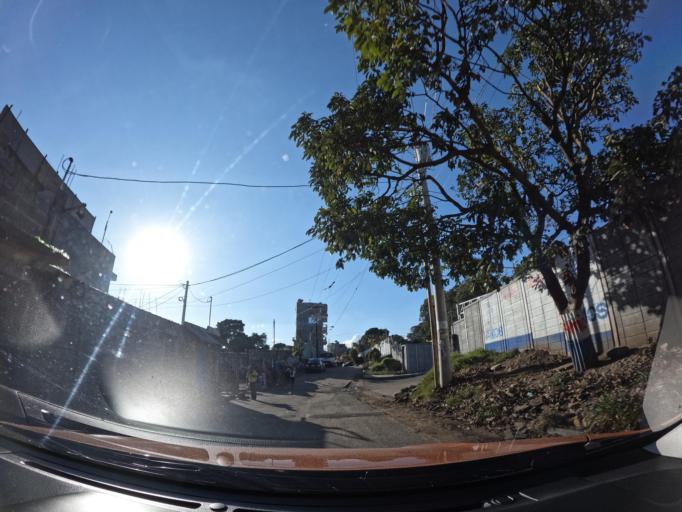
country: GT
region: Escuintla
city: Palin
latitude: 14.4077
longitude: -90.6971
